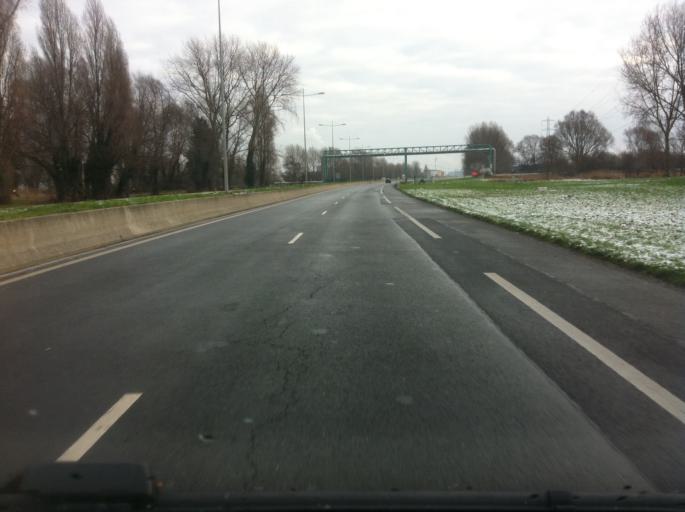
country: FR
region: Haute-Normandie
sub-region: Departement de la Seine-Maritime
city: Harfleur
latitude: 49.4875
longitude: 0.2117
